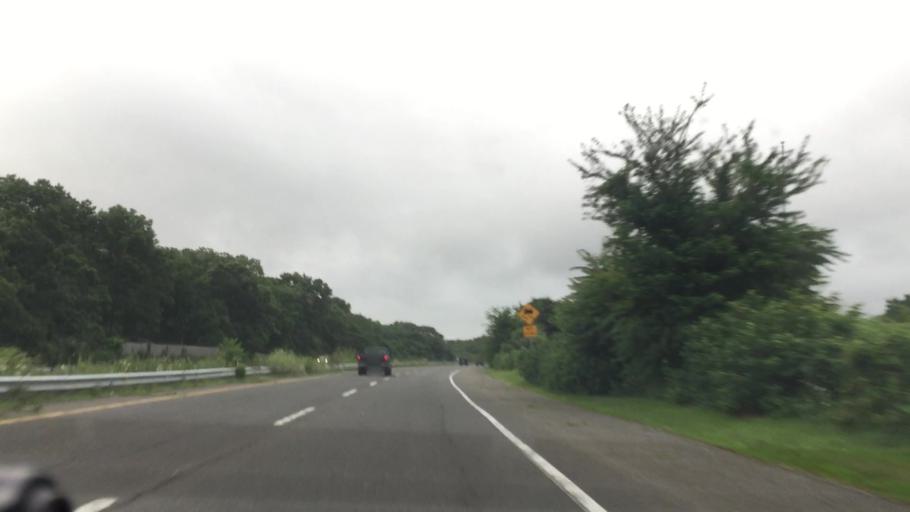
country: US
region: New York
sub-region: Suffolk County
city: Coram
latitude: 40.9005
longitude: -73.0047
